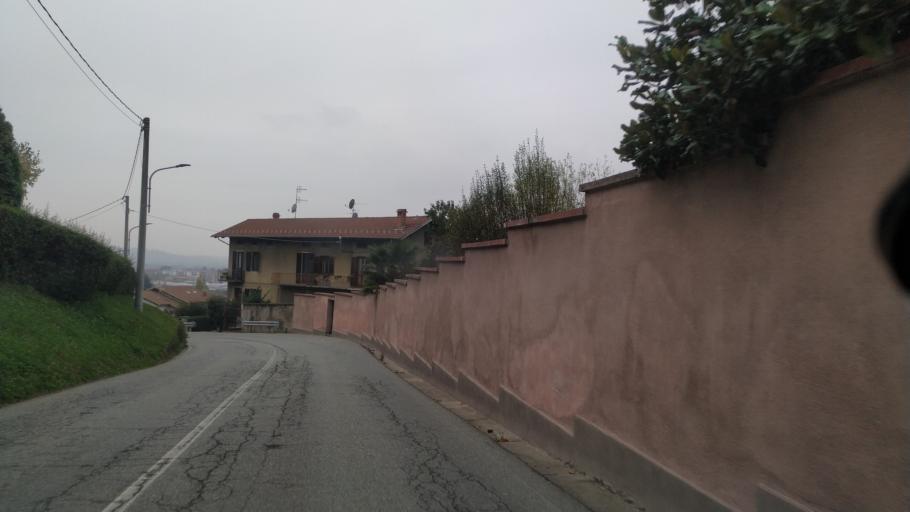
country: IT
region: Piedmont
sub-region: Provincia di Biella
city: Lessona
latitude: 45.5800
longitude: 8.1915
